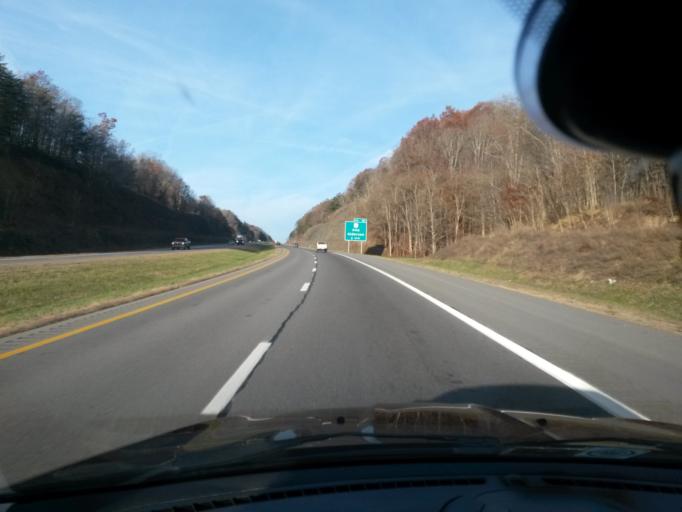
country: US
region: West Virginia
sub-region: Greenbrier County
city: Lewisburg
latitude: 37.8582
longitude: -80.5152
